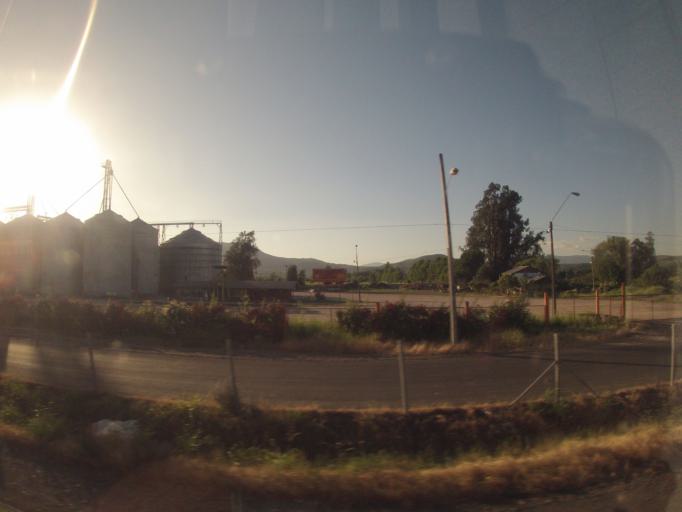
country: CL
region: O'Higgins
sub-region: Provincia de Colchagua
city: Chimbarongo
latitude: -34.6855
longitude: -71.0113
